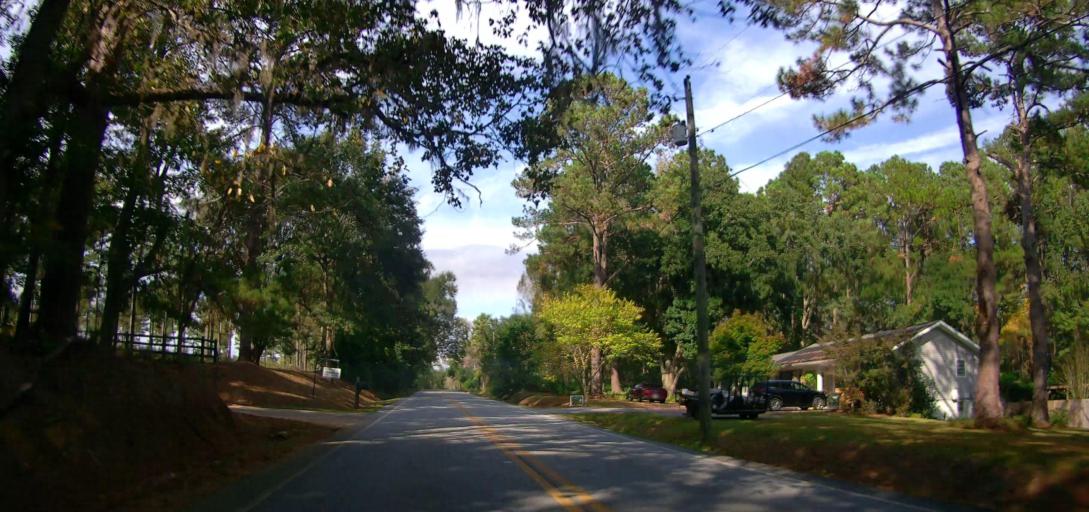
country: US
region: Georgia
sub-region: Thomas County
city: Thomasville
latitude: 30.8893
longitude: -84.0063
